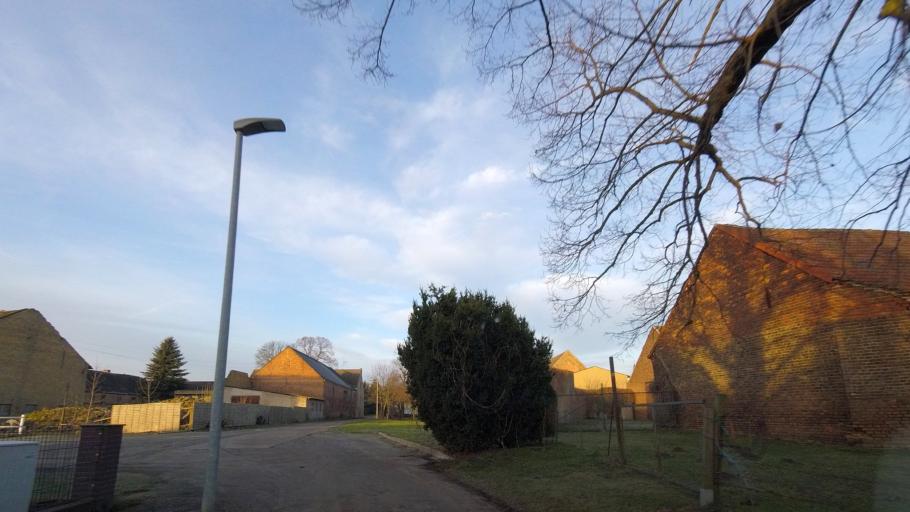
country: DE
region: Brandenburg
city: Niedergorsdorf
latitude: 51.9705
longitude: 12.9680
